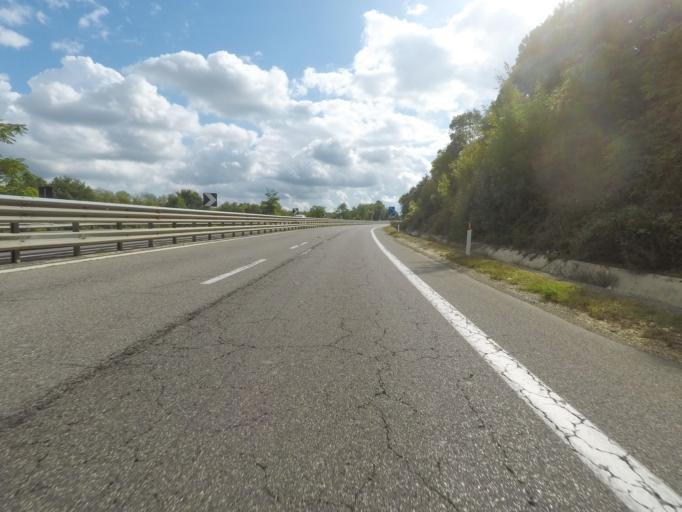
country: IT
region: Tuscany
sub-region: Provincia di Siena
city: Rapolano Terme
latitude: 43.2884
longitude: 11.6219
